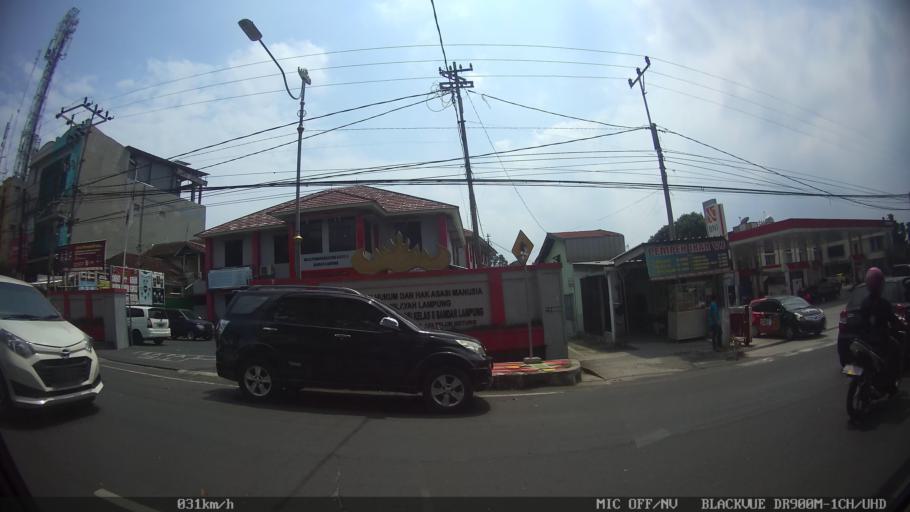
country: ID
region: Lampung
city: Bandarlampung
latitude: -5.4349
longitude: 105.2650
